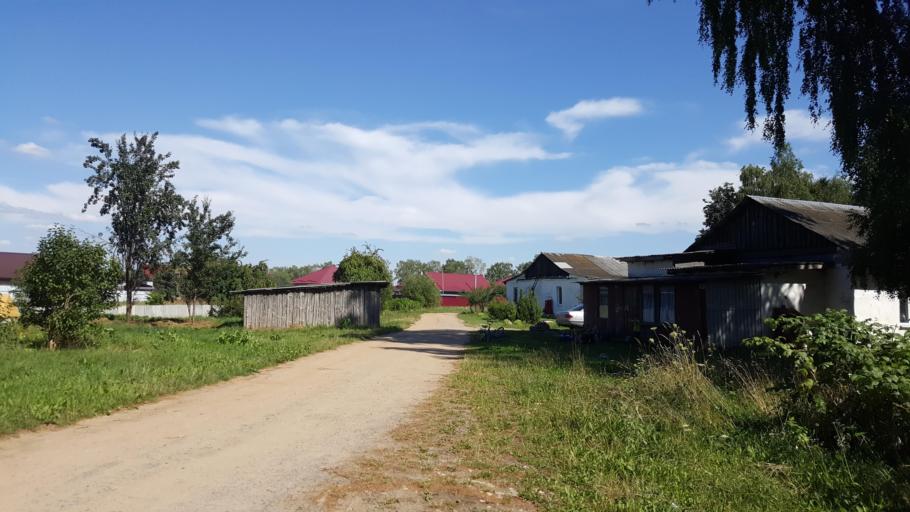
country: BY
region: Brest
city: Charnawchytsy
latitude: 52.2568
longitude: 23.5848
